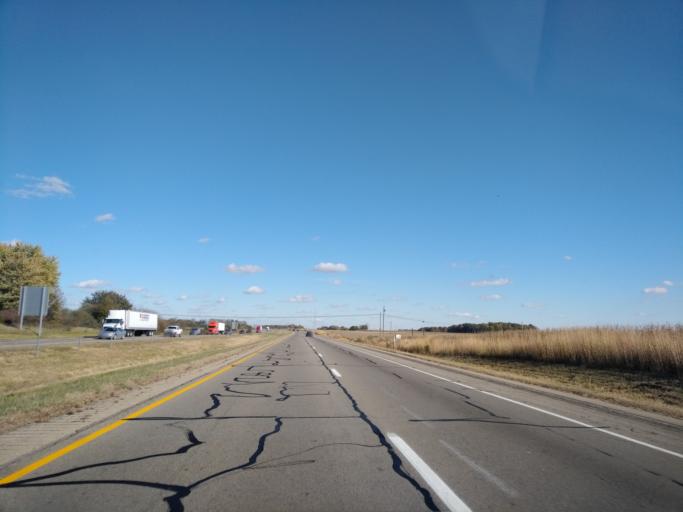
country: US
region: Indiana
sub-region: Hancock County
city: Greenfield
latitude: 39.8212
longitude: -85.7487
